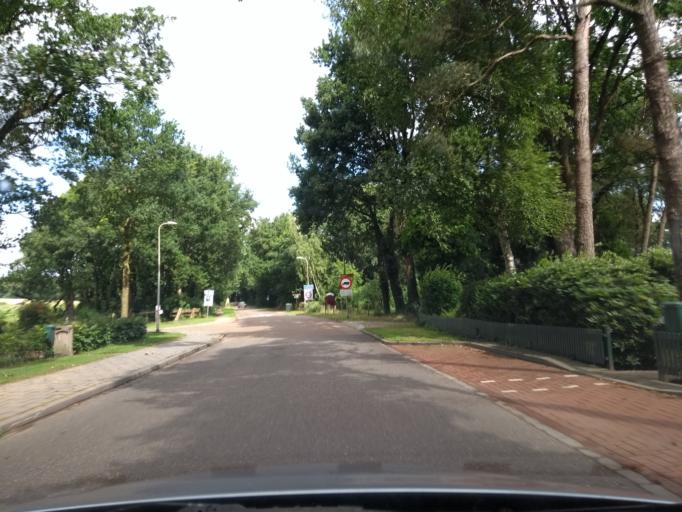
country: NL
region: Overijssel
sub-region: Gemeente Twenterand
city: Den Ham
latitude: 52.4543
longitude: 6.4129
